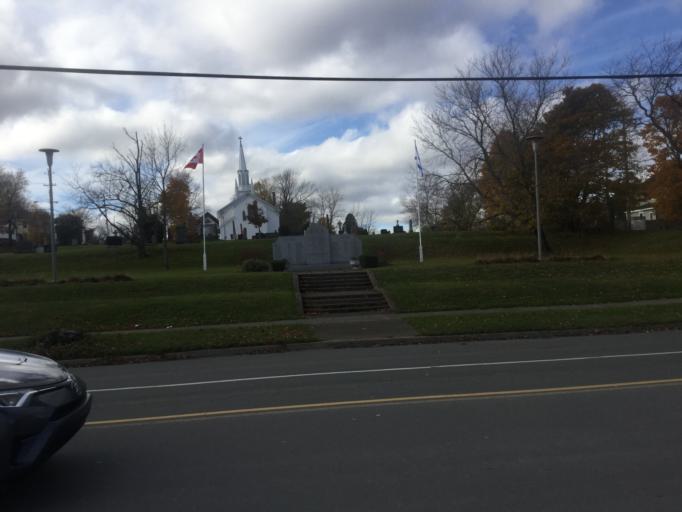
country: CA
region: Nova Scotia
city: New Glasgow
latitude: 45.5627
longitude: -62.6595
